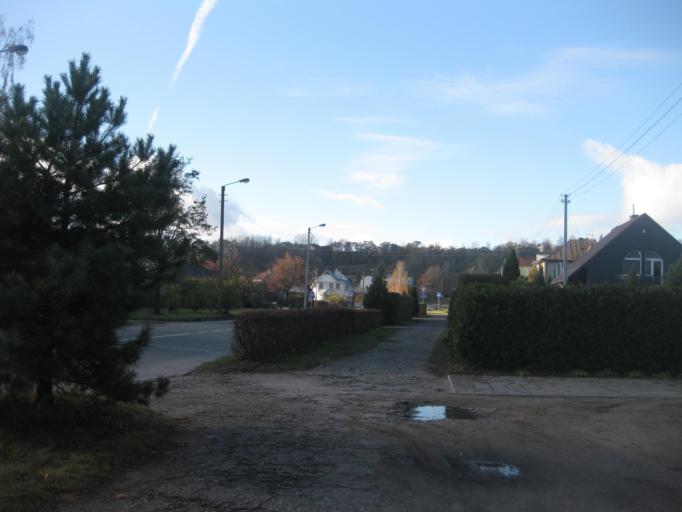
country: LT
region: Kauno apskritis
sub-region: Kaunas
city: Silainiai
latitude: 54.9187
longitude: 23.9001
